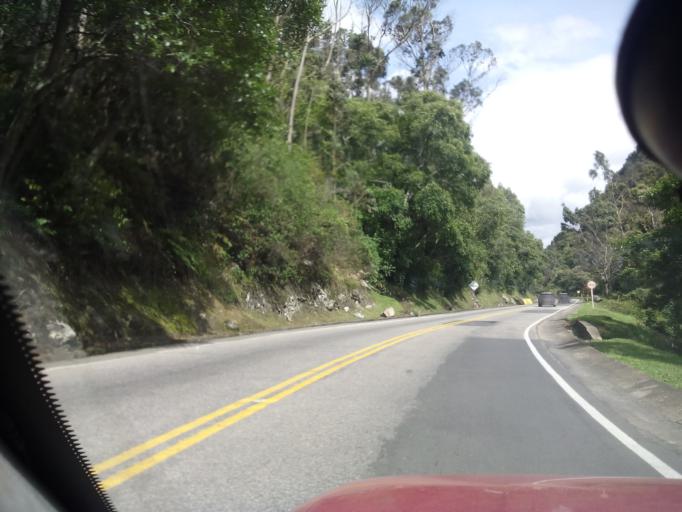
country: CO
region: Boyaca
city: Arcabuco
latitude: 5.7278
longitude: -73.3906
